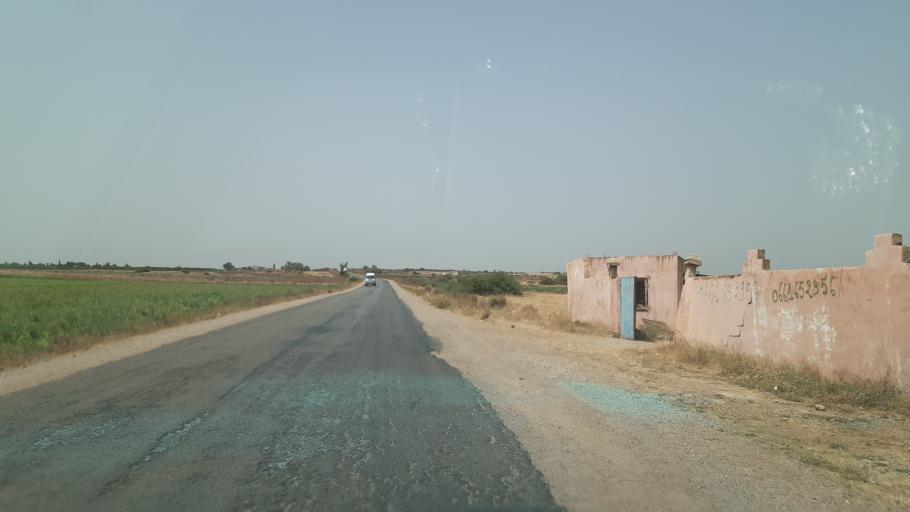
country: MA
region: Meknes-Tafilalet
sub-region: El-Hajeb
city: El Hajeb
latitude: 33.8115
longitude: -5.1880
